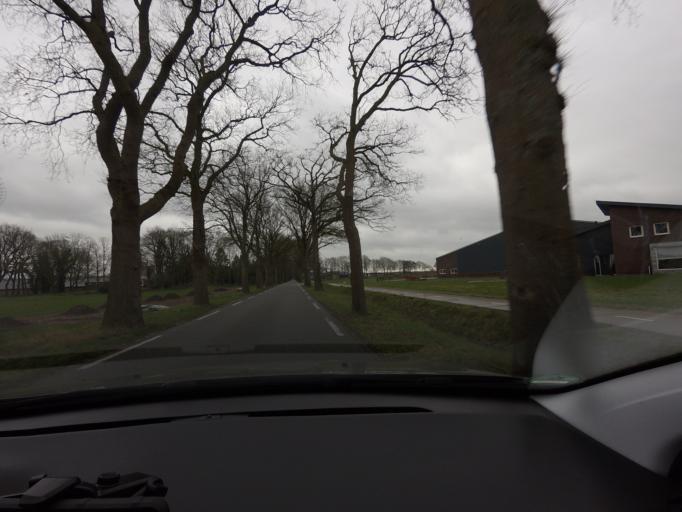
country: NL
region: Drenthe
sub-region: Gemeente Assen
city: Assen
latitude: 52.8545
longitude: 6.5690
